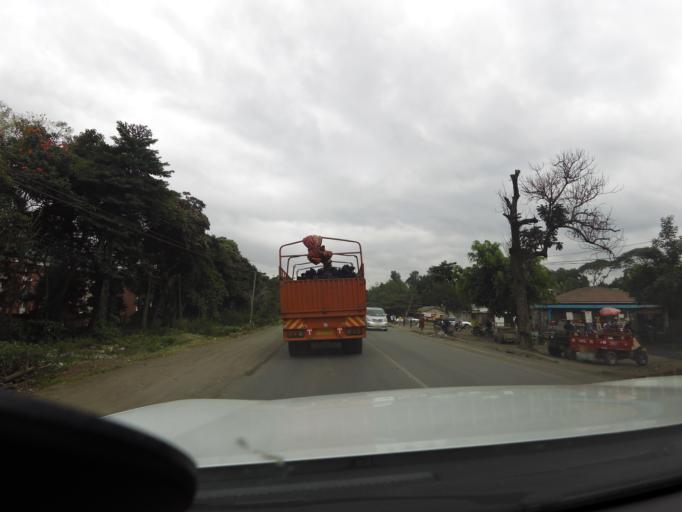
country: TZ
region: Arusha
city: Arusha
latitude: -3.3628
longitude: 36.6781
